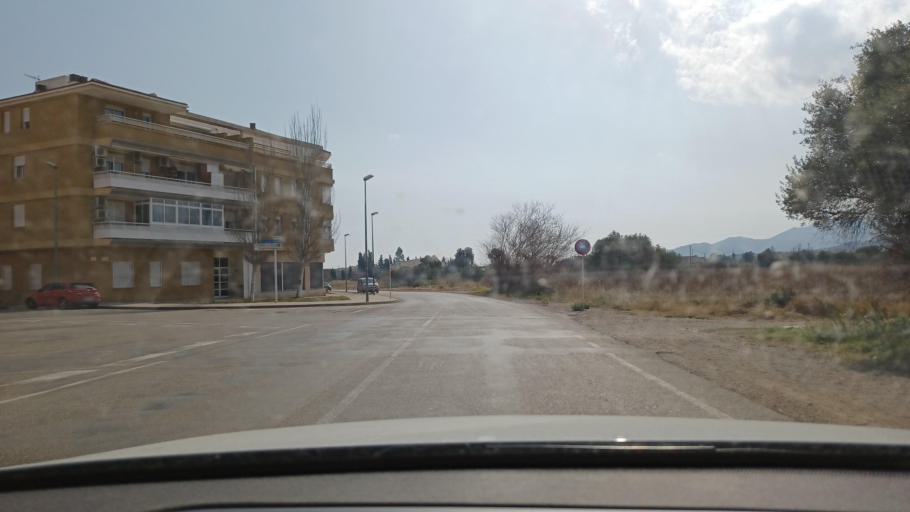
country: ES
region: Catalonia
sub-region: Provincia de Tarragona
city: Amposta
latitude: 40.7043
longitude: 0.5719
